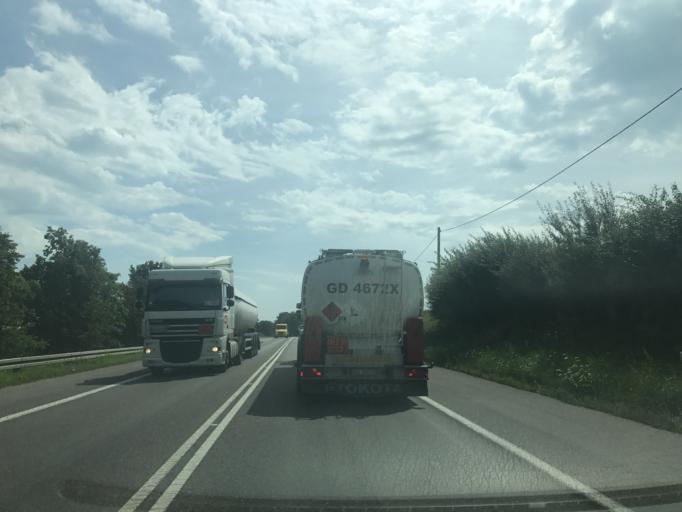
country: PL
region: Warmian-Masurian Voivodeship
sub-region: Powiat ostrodzki
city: Ostroda
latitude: 53.6669
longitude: 20.0386
